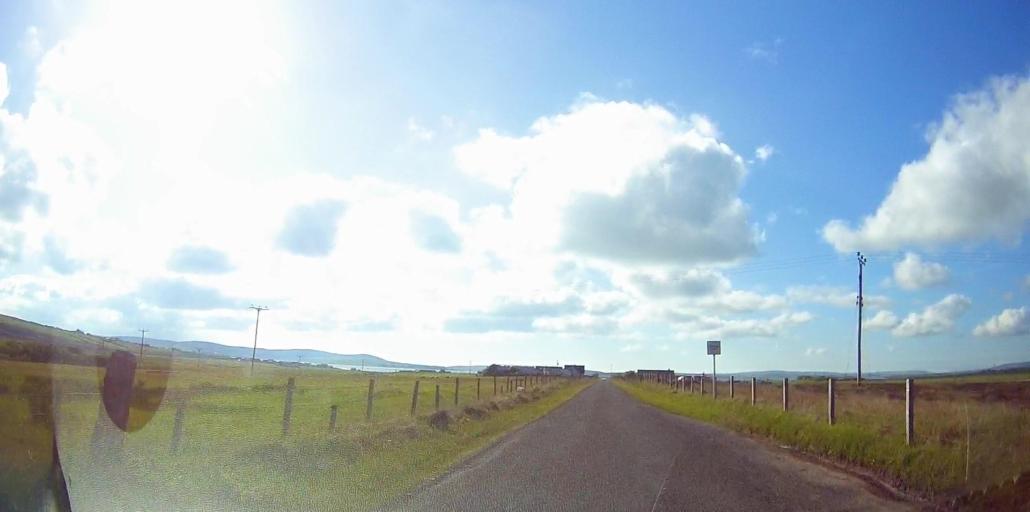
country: GB
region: Scotland
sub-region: Orkney Islands
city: Stromness
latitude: 58.9840
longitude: -3.1866
